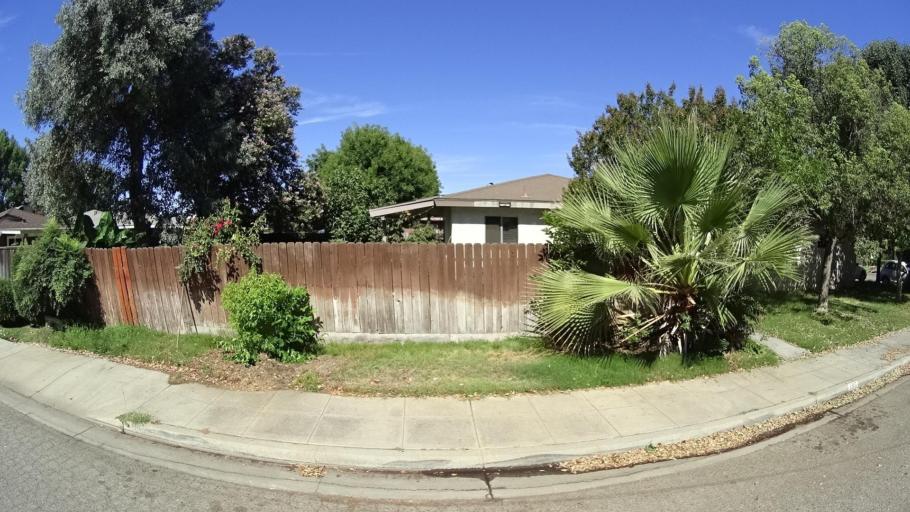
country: US
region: California
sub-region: Fresno County
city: Sunnyside
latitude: 36.7448
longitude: -119.7047
